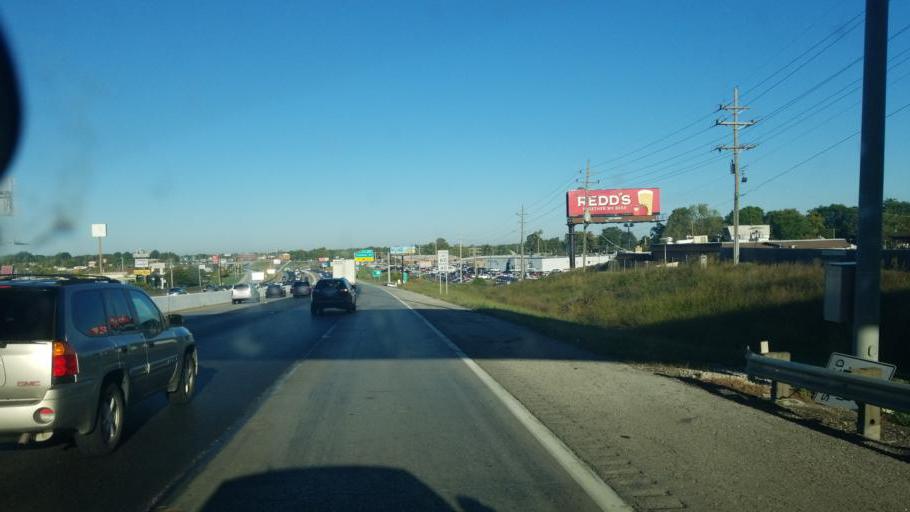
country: US
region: Missouri
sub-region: Saint Charles County
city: Saint Charles
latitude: 38.7819
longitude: -90.5193
